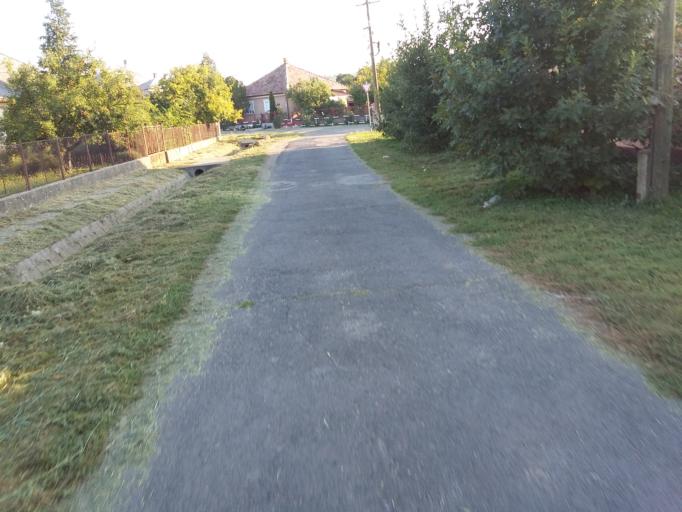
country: HU
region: Borsod-Abauj-Zemplen
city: Bekecs
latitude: 48.1601
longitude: 21.1816
